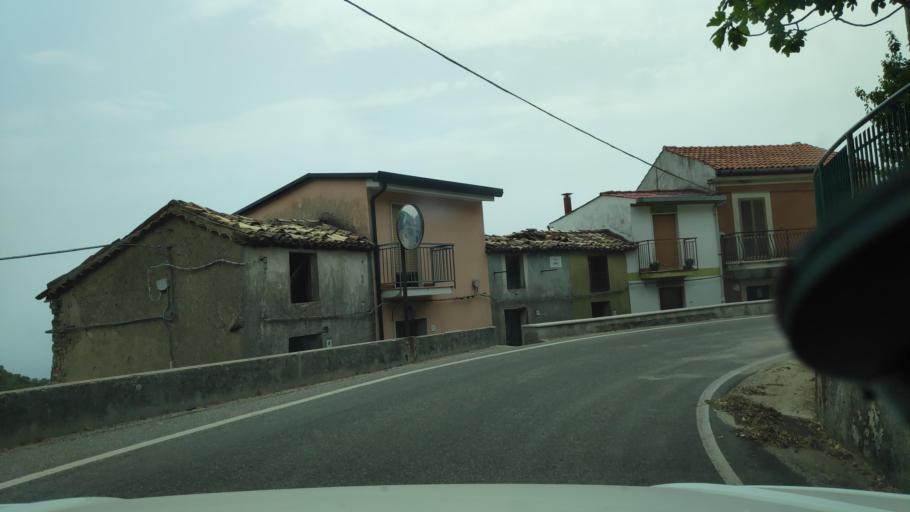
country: IT
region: Calabria
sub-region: Provincia di Catanzaro
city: San Sostene
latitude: 38.6394
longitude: 16.4851
